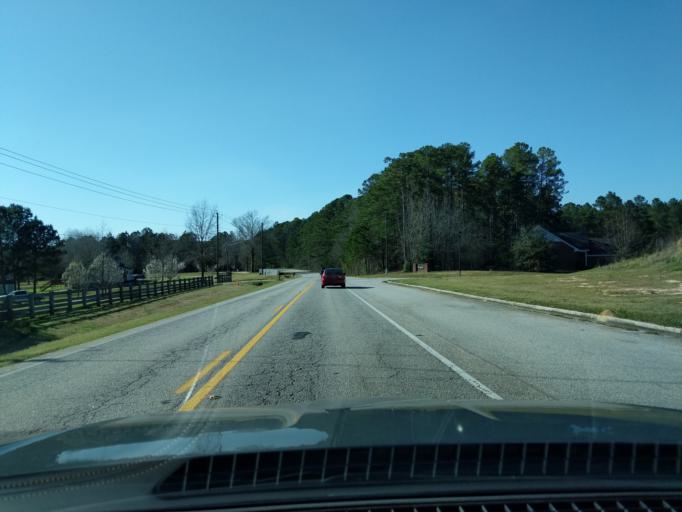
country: US
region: Georgia
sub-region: Columbia County
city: Grovetown
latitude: 33.4539
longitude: -82.2259
